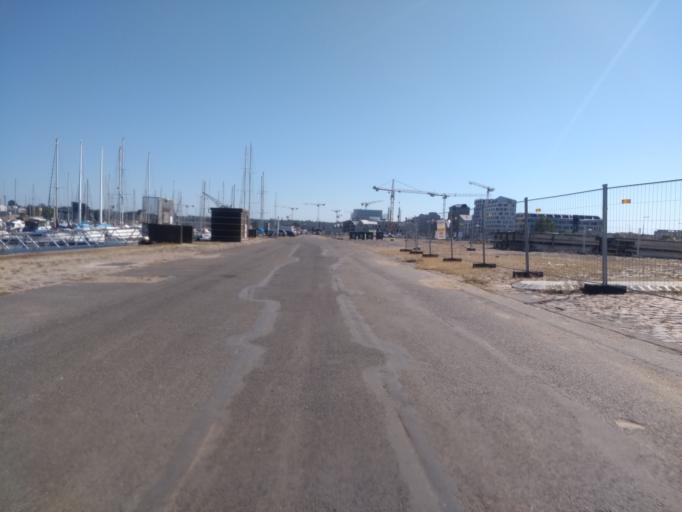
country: FR
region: Aquitaine
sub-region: Departement de la Gironde
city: Le Bouscat
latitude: 44.8687
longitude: -0.5632
